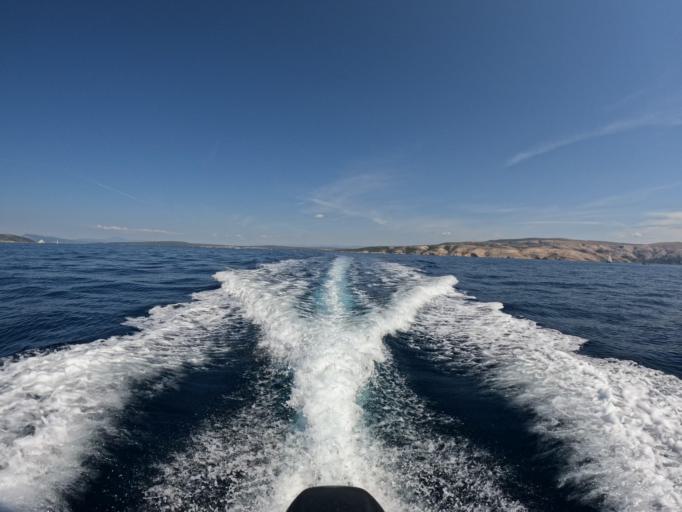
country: HR
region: Primorsko-Goranska
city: Punat
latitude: 44.9378
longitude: 14.6159
